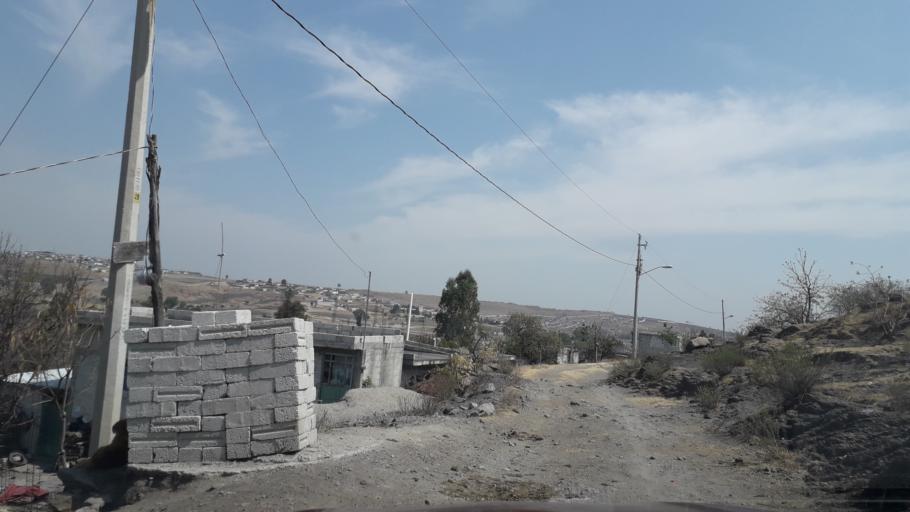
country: MX
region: Puebla
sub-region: Puebla
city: San Andres Azumiatla
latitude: 18.9186
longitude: -98.2593
